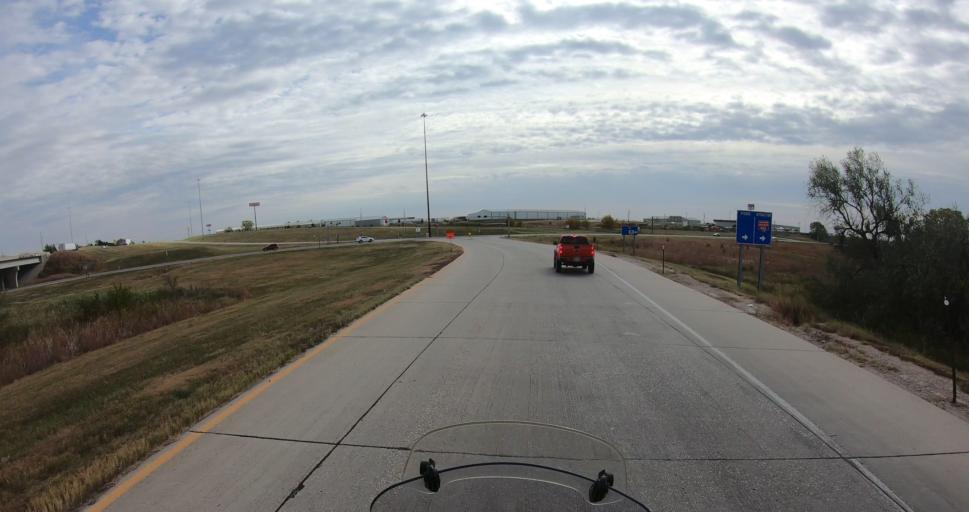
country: US
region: Nebraska
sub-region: Lancaster County
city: Lincoln
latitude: 40.8959
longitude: -96.6451
